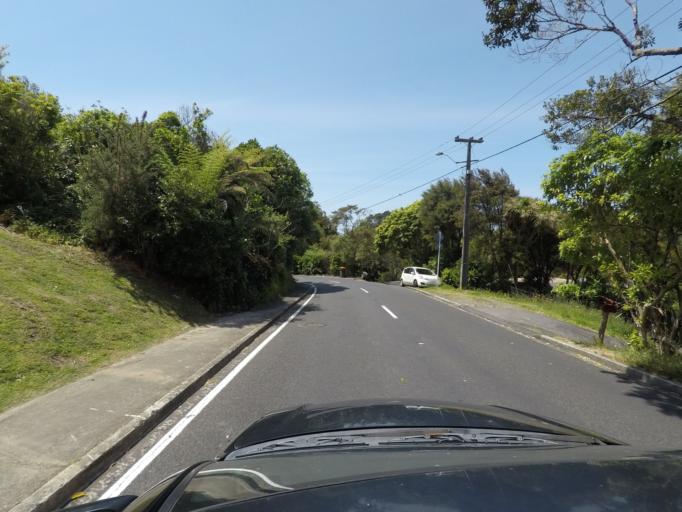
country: NZ
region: Auckland
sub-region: Auckland
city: Titirangi
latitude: -36.9665
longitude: 174.6380
